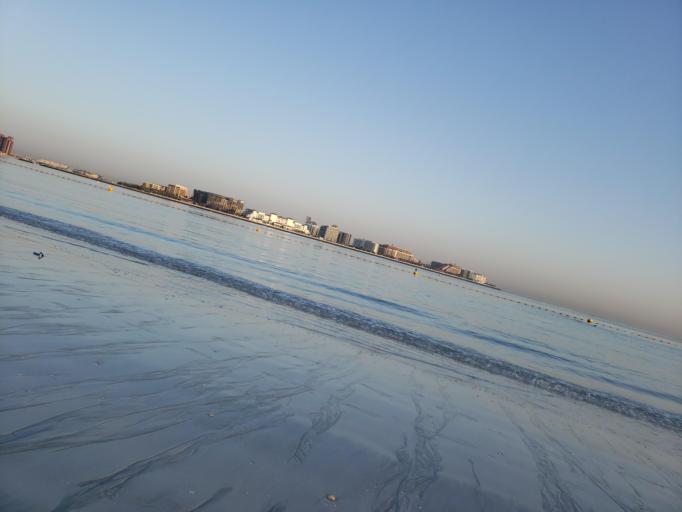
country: AE
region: Dubai
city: Dubai
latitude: 25.1184
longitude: 55.1682
